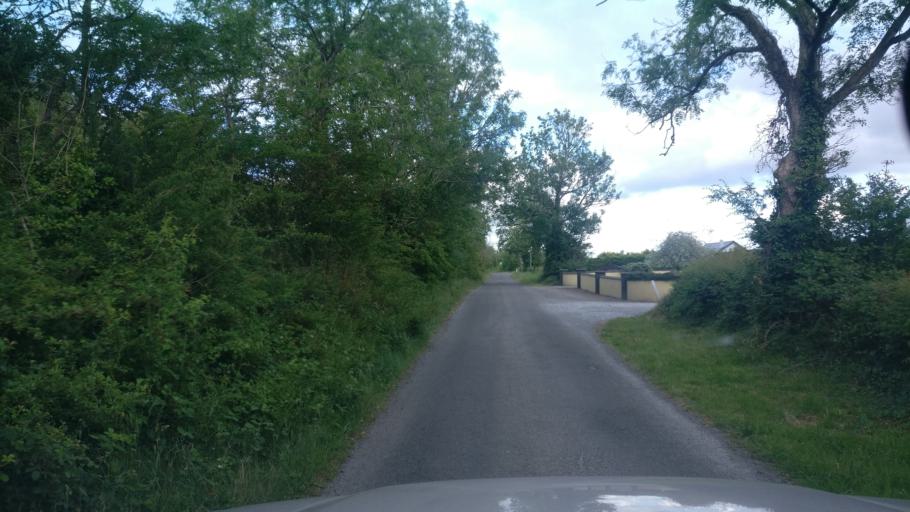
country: IE
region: Connaught
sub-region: County Galway
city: Portumna
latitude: 53.1993
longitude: -8.3312
